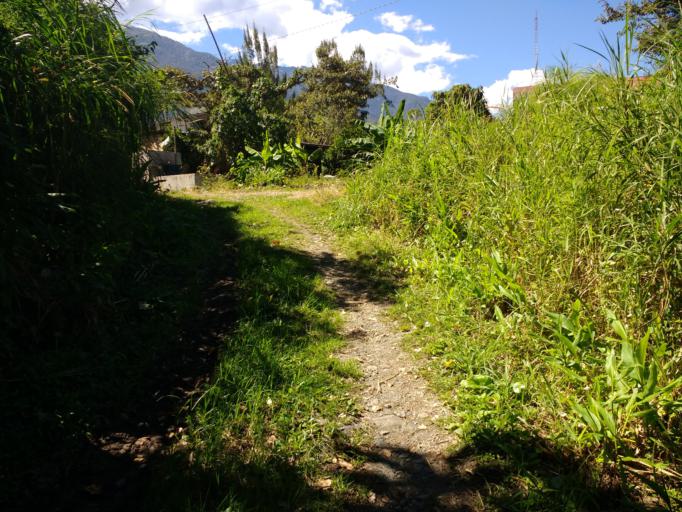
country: PE
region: Cusco
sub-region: Provincia de La Convencion
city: Maranura
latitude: -12.9997
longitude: -72.5327
